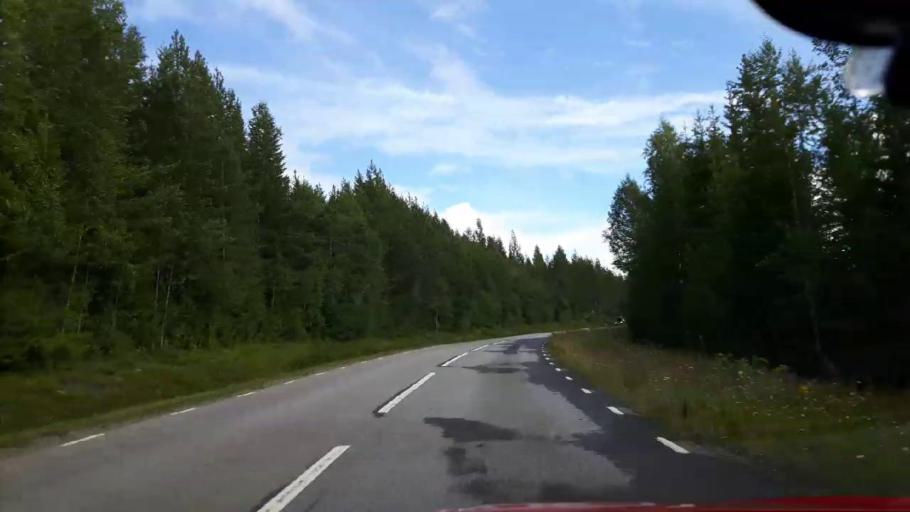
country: SE
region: Jaemtland
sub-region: Stroemsunds Kommun
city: Stroemsund
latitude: 64.3475
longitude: 15.0782
